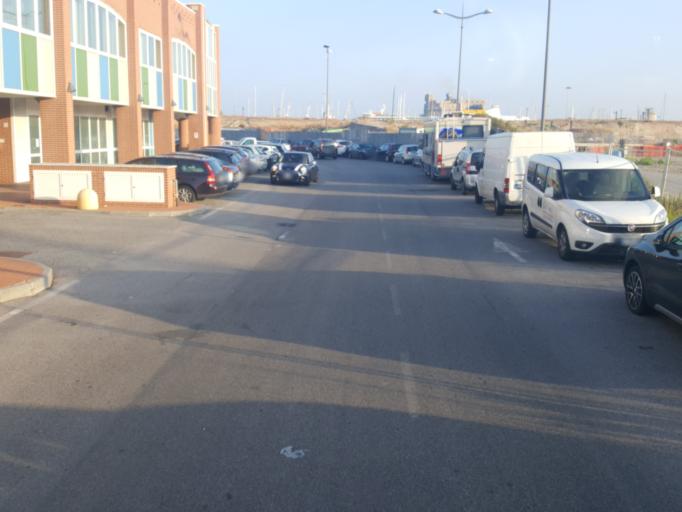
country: IT
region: Tuscany
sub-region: Provincia di Livorno
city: Livorno
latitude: 43.5443
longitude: 10.3013
